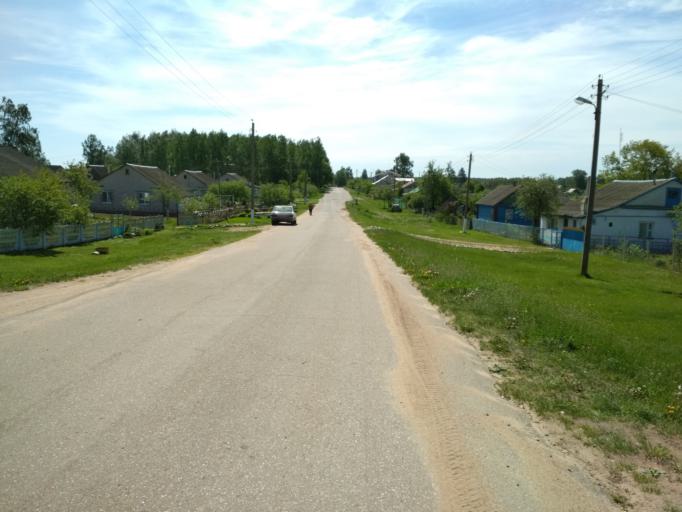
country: BY
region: Grodnenskaya
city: Mir
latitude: 53.3841
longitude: 26.3630
